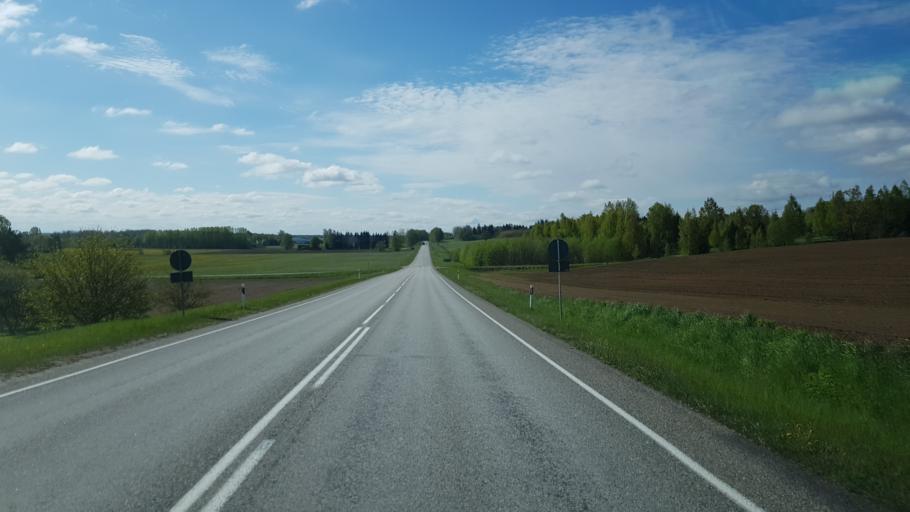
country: EE
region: Valgamaa
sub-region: Valga linn
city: Valga
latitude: 57.8997
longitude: 26.0507
